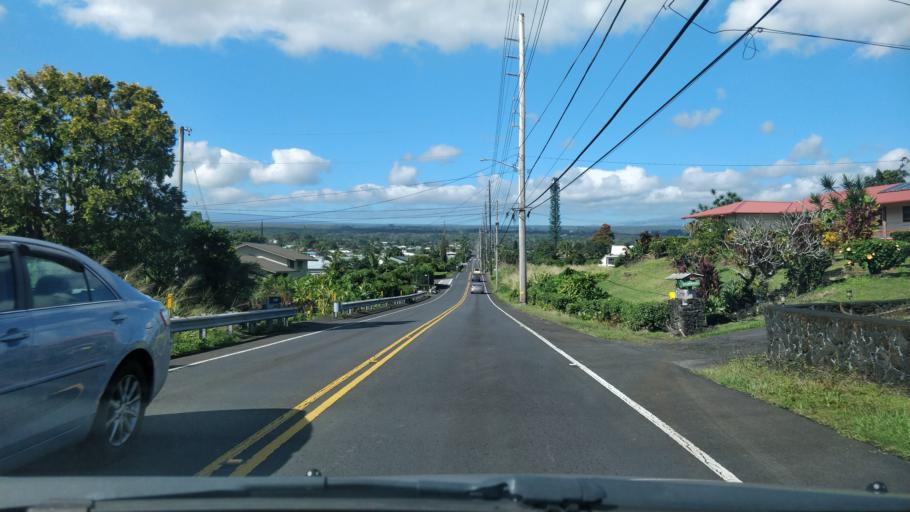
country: US
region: Hawaii
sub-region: Hawaii County
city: Hilo
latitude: 19.6830
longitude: -155.0924
